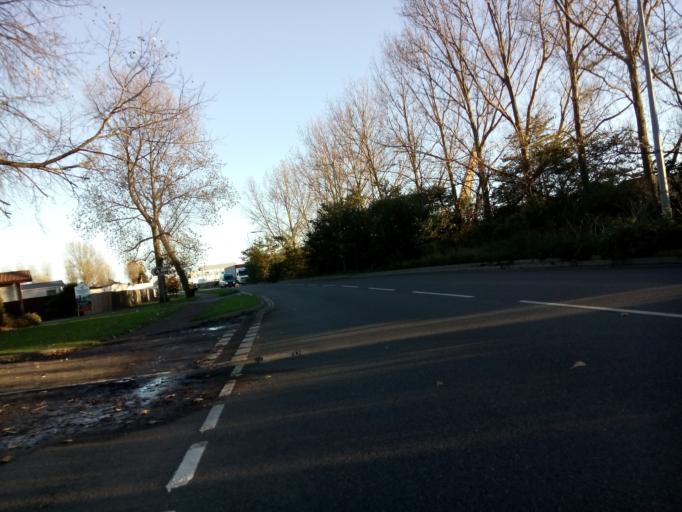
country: GB
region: England
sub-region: Suffolk
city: Felixstowe
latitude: 51.9549
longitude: 1.3292
